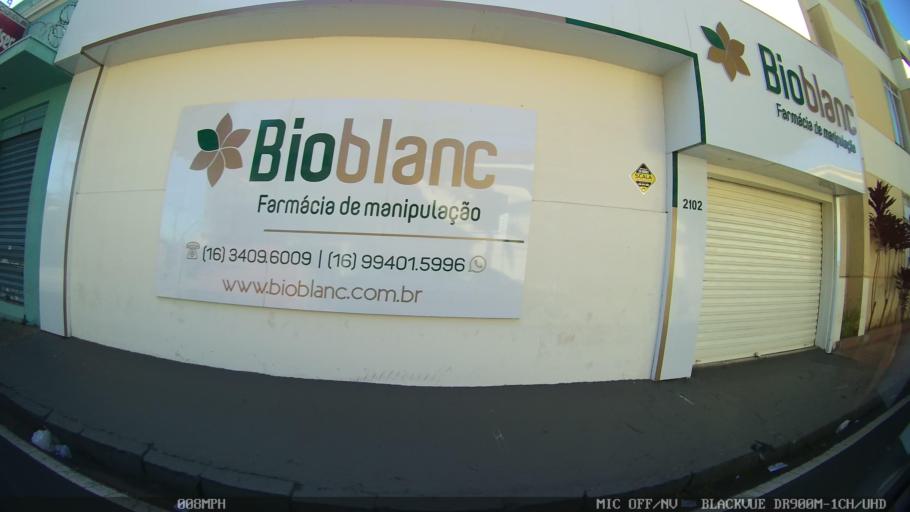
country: BR
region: Sao Paulo
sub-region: Franca
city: Franca
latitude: -20.5352
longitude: -47.4024
